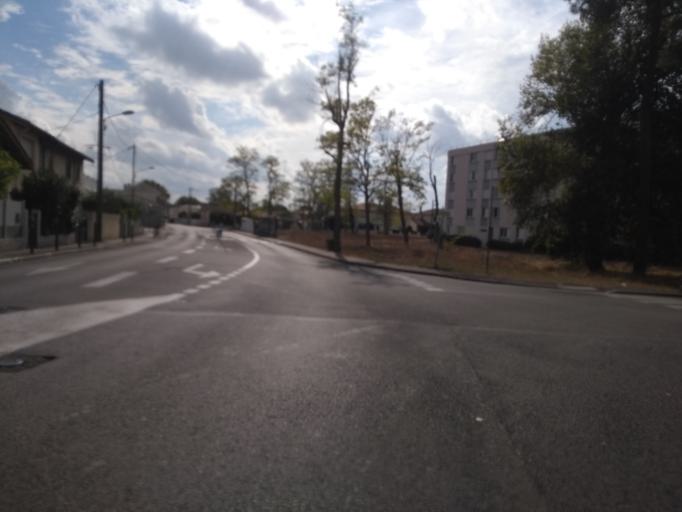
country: FR
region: Aquitaine
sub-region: Departement de la Gironde
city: Merignac
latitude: 44.8218
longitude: -0.6249
